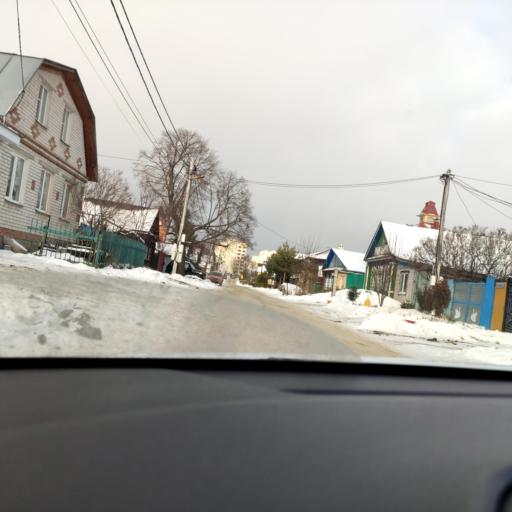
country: RU
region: Tatarstan
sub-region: Gorod Kazan'
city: Kazan
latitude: 55.7928
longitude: 49.0596
